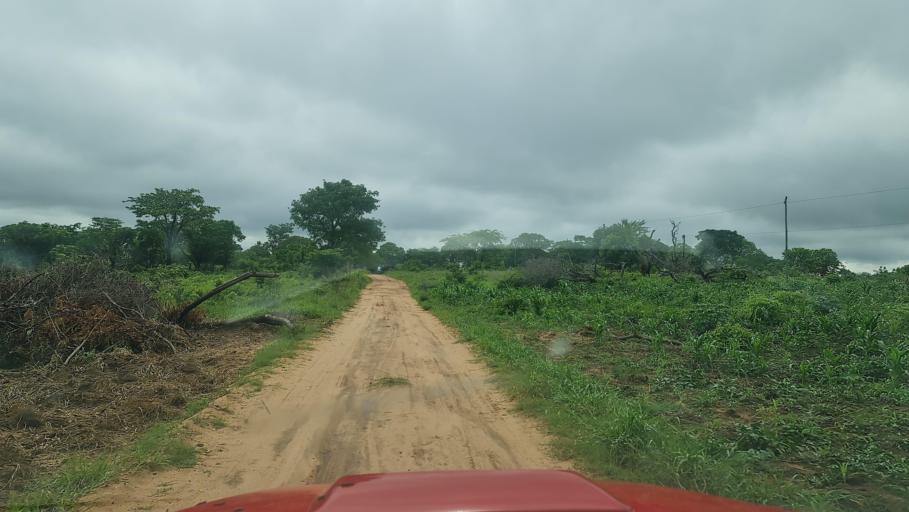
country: MW
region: Southern Region
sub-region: Nsanje District
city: Nsanje
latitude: -17.1928
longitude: 35.8548
